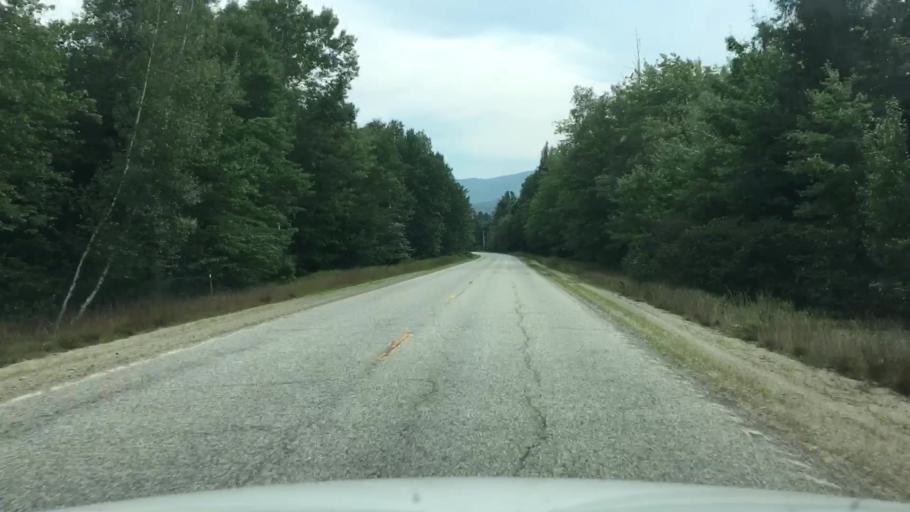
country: US
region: Maine
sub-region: Oxford County
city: Rumford
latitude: 44.6013
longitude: -70.7368
